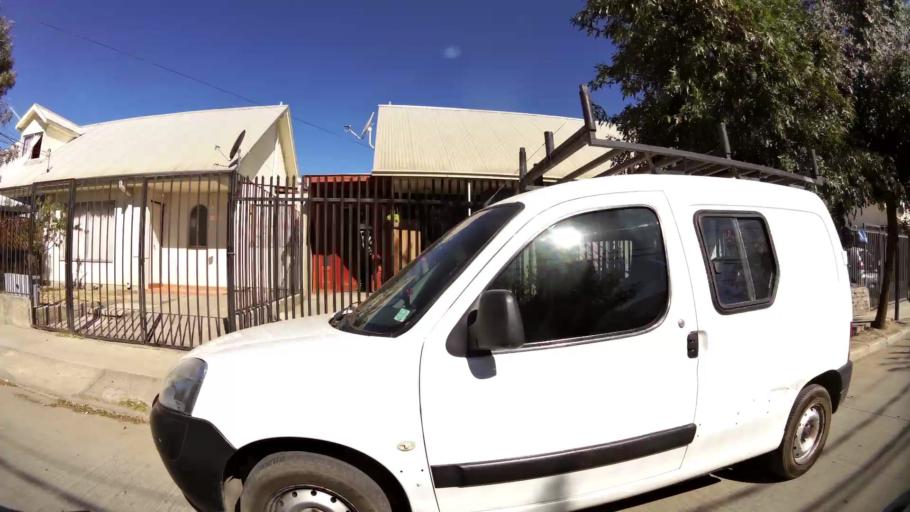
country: CL
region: O'Higgins
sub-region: Provincia de Cachapoal
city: Rancagua
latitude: -34.1837
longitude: -70.7725
